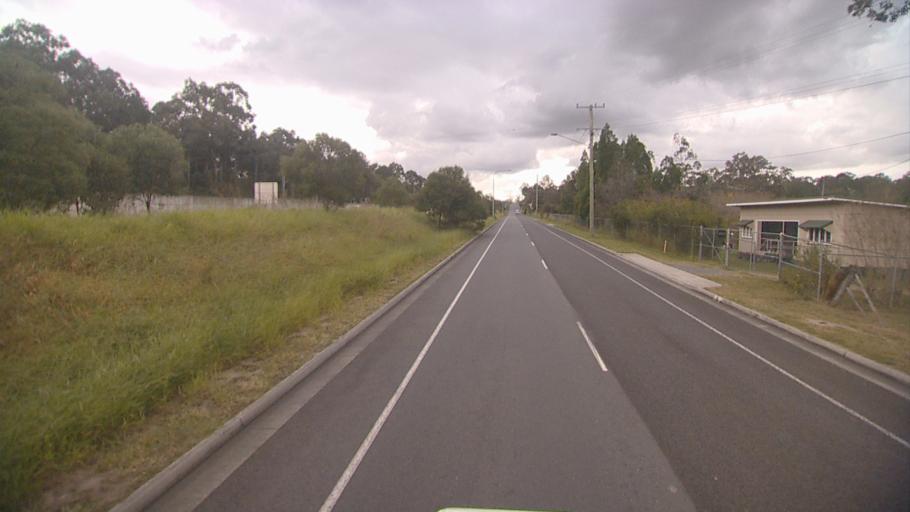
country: AU
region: Queensland
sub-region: Logan
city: Park Ridge South
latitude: -27.7209
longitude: 153.0318
